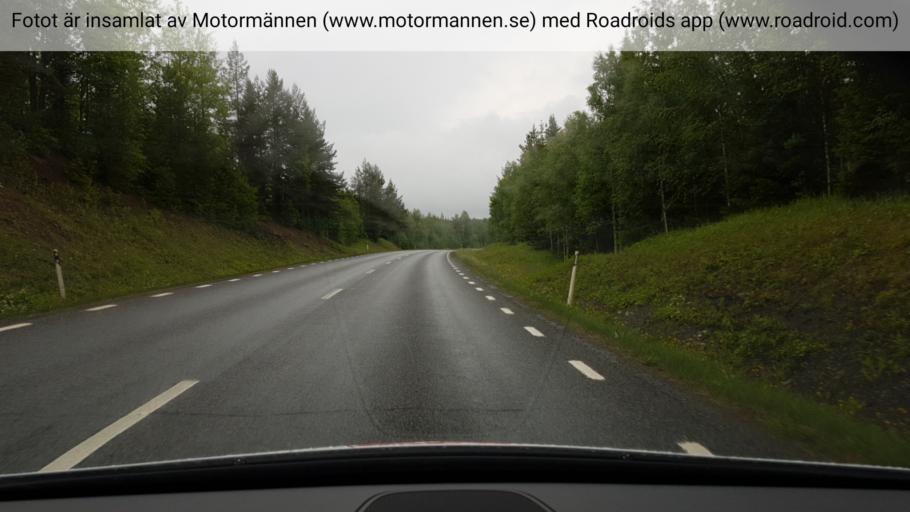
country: SE
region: Jaemtland
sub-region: OEstersunds Kommun
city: Lit
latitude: 63.4035
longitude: 15.0571
